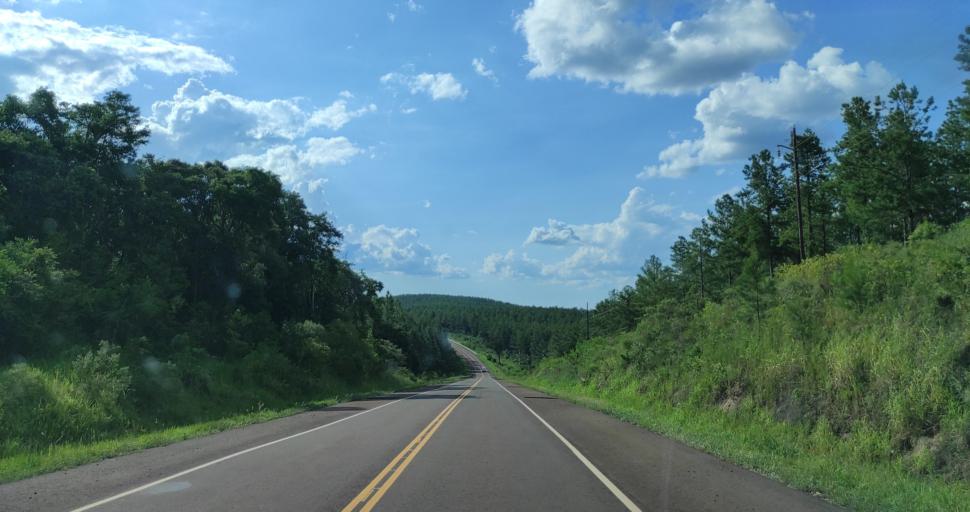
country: AR
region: Misiones
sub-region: Departamento de San Pedro
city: San Pedro
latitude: -26.3569
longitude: -53.9564
